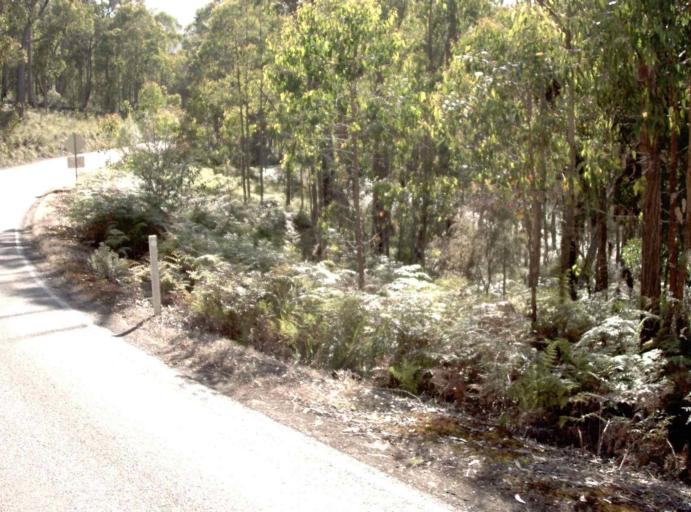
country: AU
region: Victoria
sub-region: East Gippsland
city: Lakes Entrance
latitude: -37.5562
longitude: 148.5594
